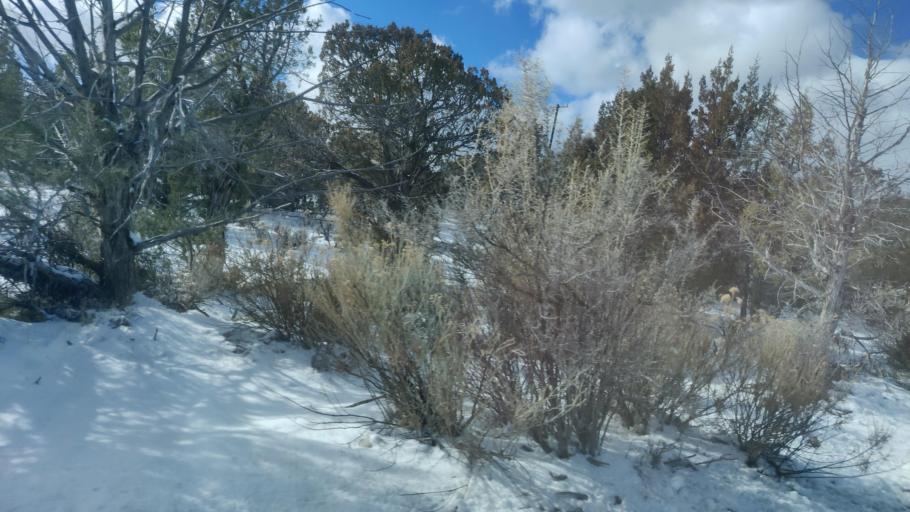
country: US
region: Colorado
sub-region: Mesa County
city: Palisade
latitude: 39.2110
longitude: -108.1479
